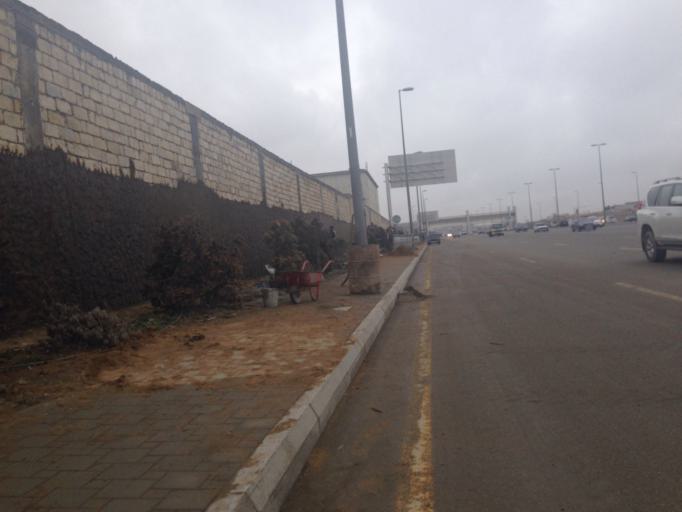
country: AZ
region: Baki
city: Baku
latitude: 40.4226
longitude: 49.8721
